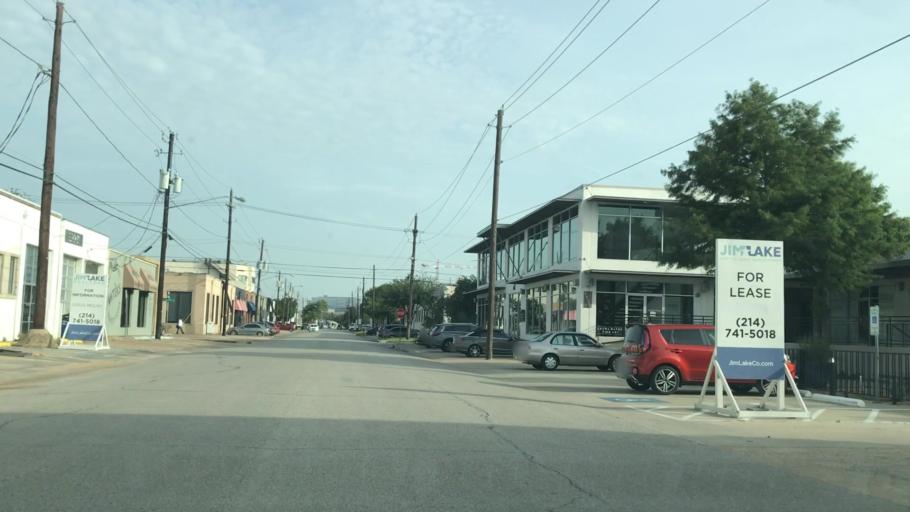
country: US
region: Texas
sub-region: Dallas County
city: Dallas
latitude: 32.7880
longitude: -96.8173
